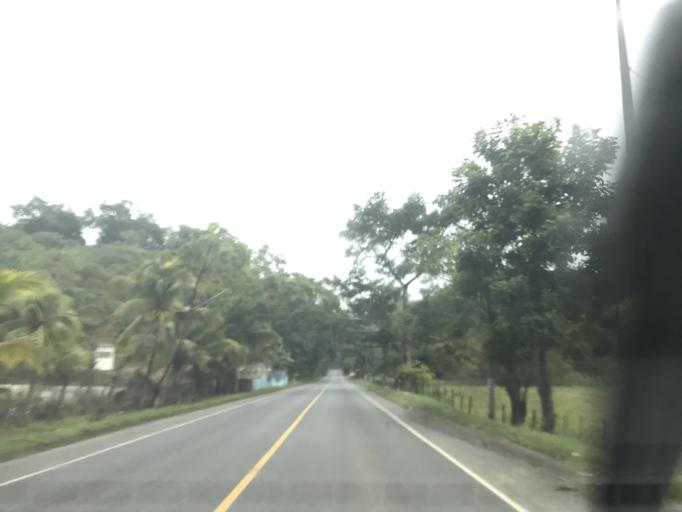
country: GT
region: Izabal
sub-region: Municipio de Puerto Barrios
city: Puerto Barrios
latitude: 15.6679
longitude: -88.5613
